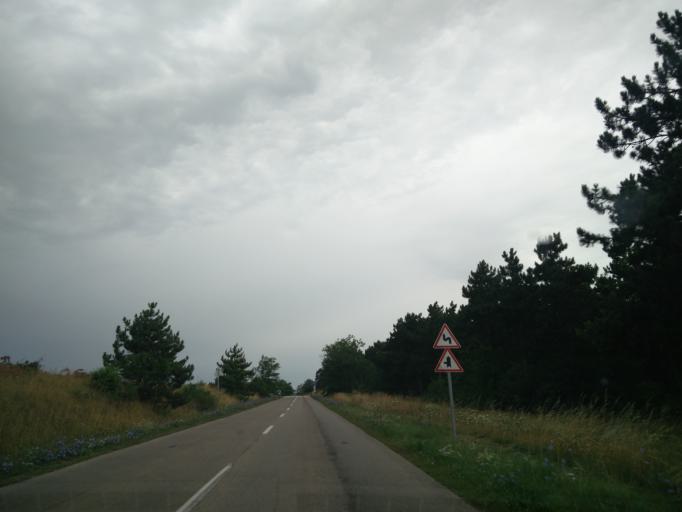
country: HU
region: Fejer
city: Etyek
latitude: 47.4439
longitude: 18.7323
